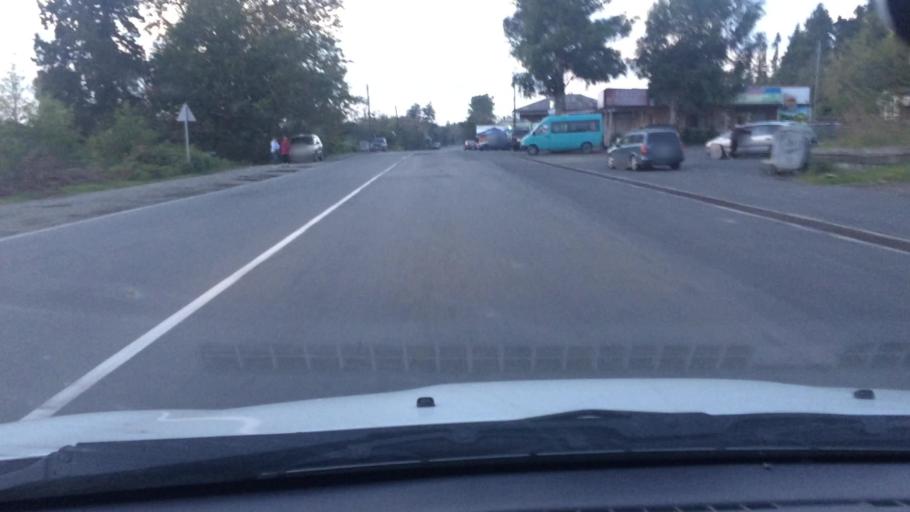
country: GE
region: Guria
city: Urek'i
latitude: 41.9994
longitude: 41.7801
